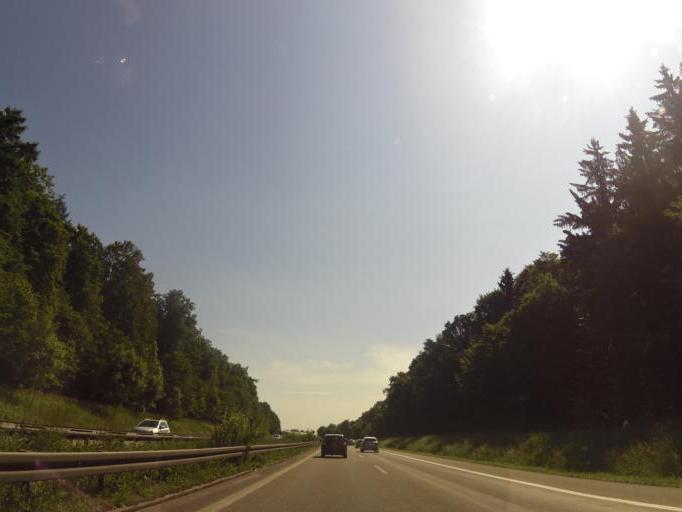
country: DE
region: Baden-Wuerttemberg
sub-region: Tuebingen Region
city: Bernstadt
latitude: 48.4543
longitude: 10.0651
